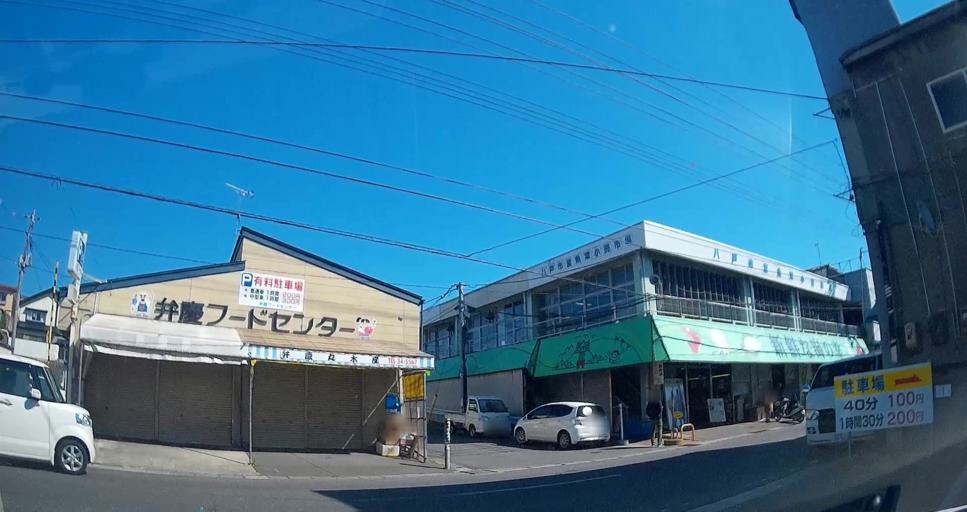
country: JP
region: Aomori
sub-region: Hachinohe Shi
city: Uchimaru
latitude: 40.5233
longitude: 141.5270
